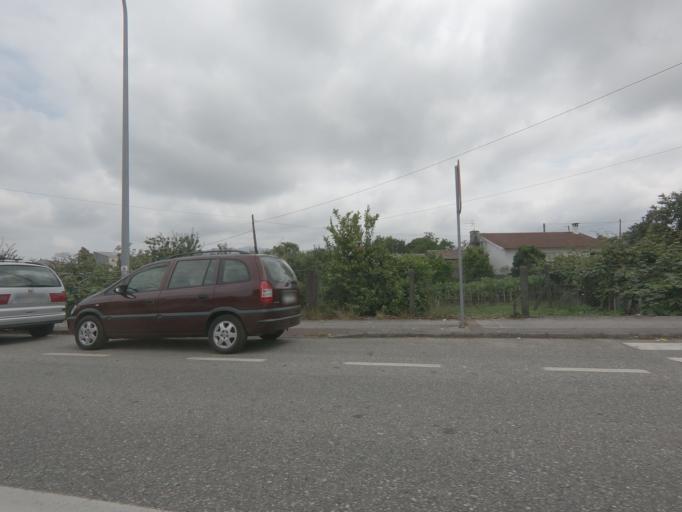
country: PT
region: Viana do Castelo
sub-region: Vila Nova de Cerveira
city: Vila Nova de Cerveira
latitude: 41.9464
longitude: -8.7767
